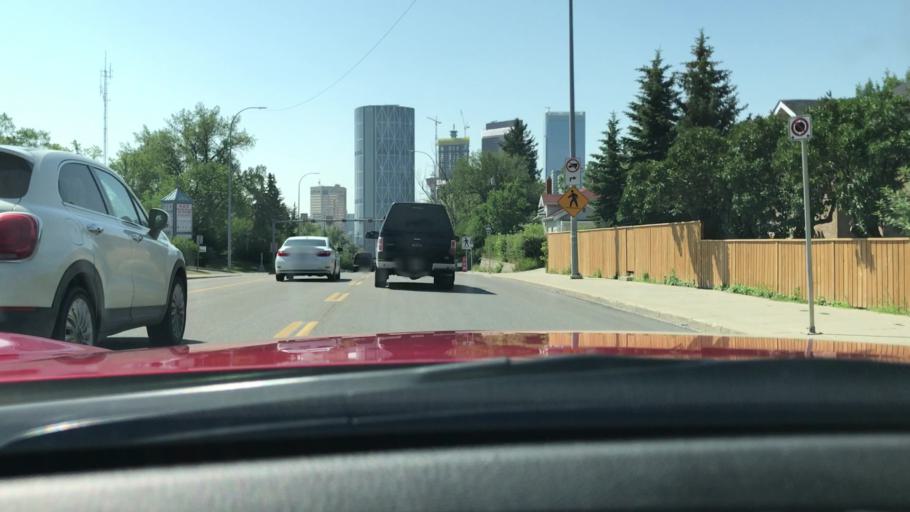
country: CA
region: Alberta
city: Calgary
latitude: 51.0597
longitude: -114.0626
